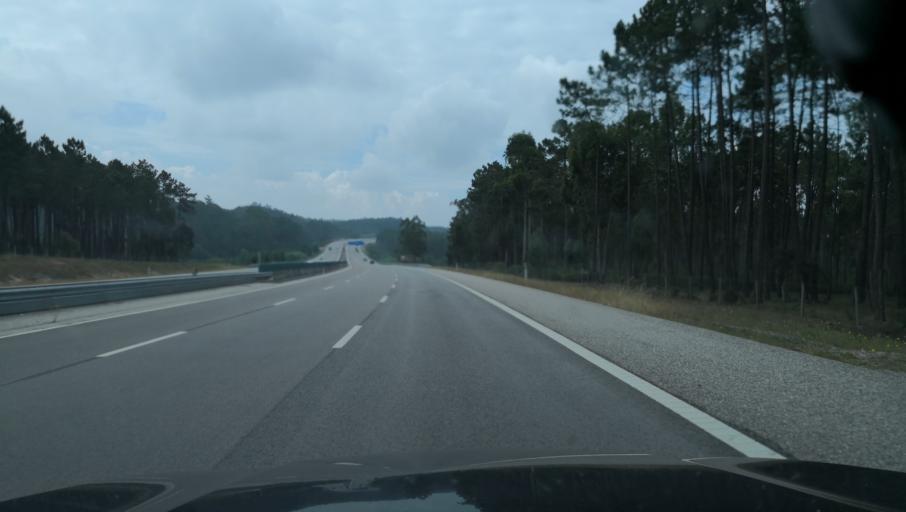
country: PT
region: Leiria
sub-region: Leiria
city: Souto da Carpalhosa
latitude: 39.8700
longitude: -8.8247
